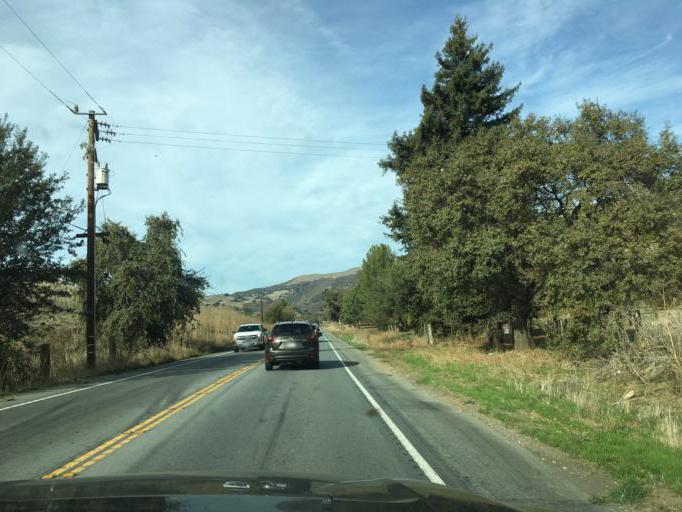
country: US
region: California
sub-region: San Benito County
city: Hollister
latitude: 36.9793
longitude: -121.4381
